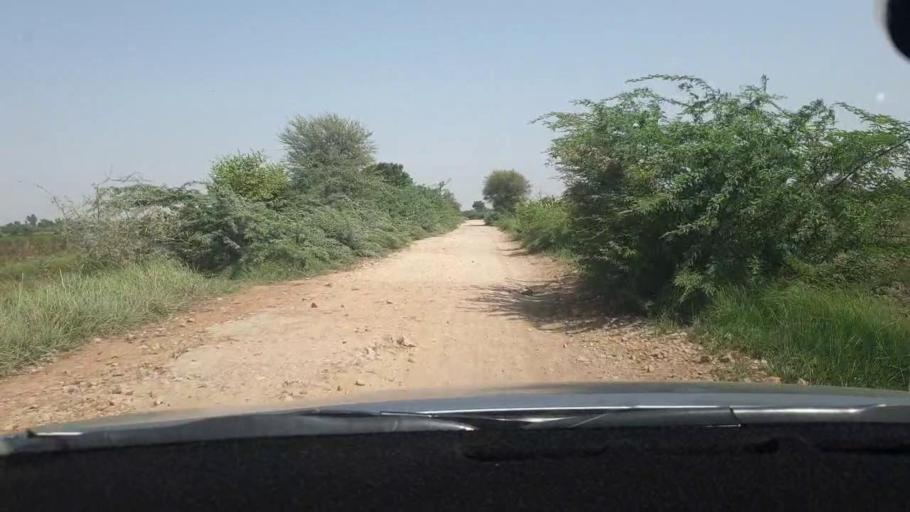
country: PK
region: Sindh
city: Tando Mittha Khan
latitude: 25.8455
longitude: 69.4360
